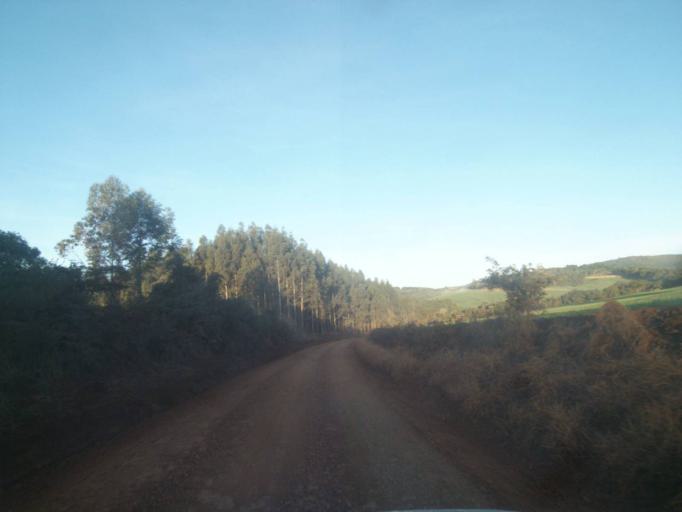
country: BR
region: Parana
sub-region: Tibagi
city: Tibagi
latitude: -24.5254
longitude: -50.4946
